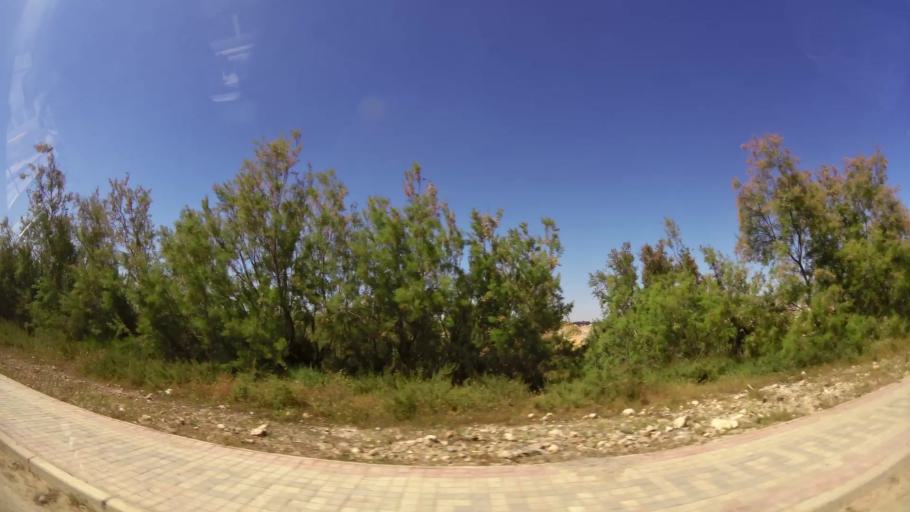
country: MA
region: Oriental
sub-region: Berkane-Taourirt
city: Madagh
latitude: 35.1040
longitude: -2.3144
